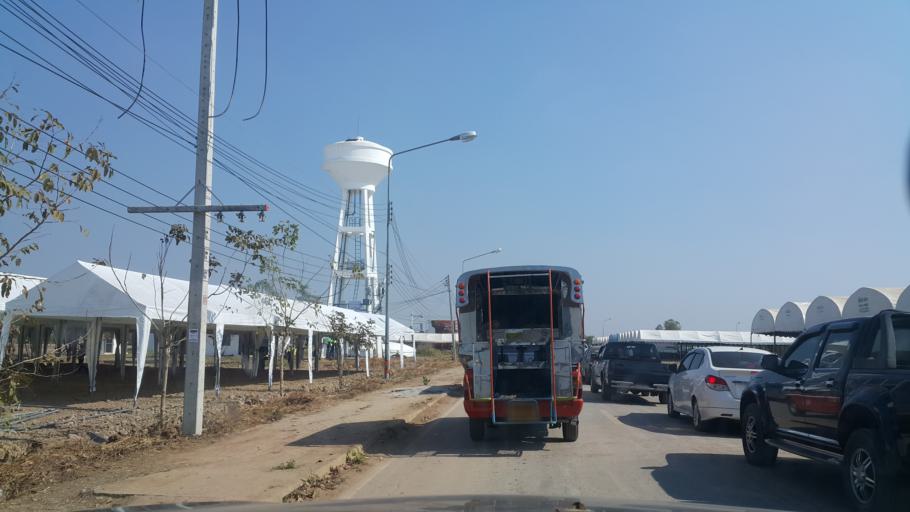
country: TH
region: Khon Kaen
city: Khon Kaen
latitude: 16.5133
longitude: 102.8702
